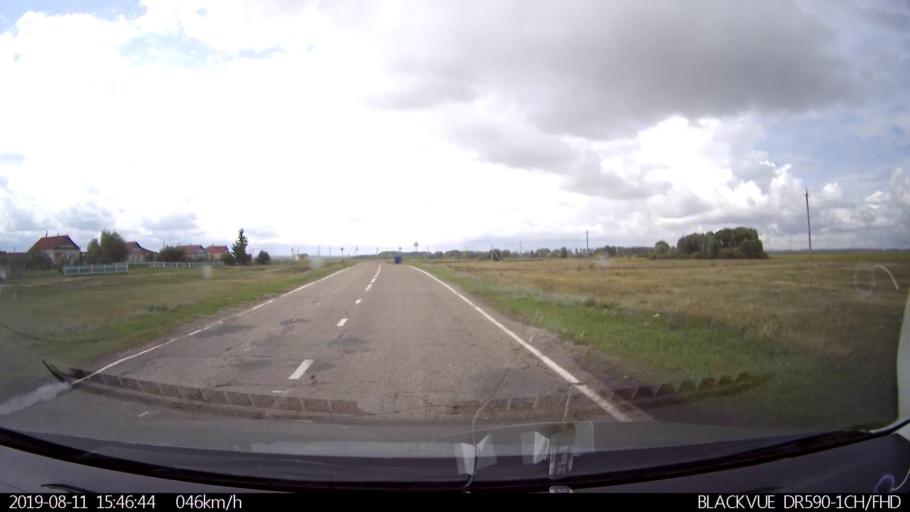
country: RU
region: Ulyanovsk
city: Ignatovka
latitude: 53.8839
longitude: 47.6546
